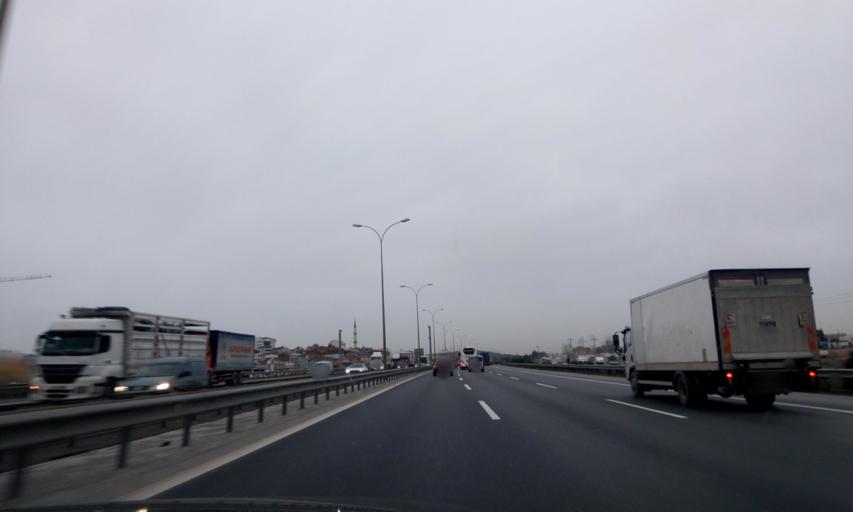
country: TR
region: Kocaeli
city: Gebze
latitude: 40.8096
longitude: 29.4636
